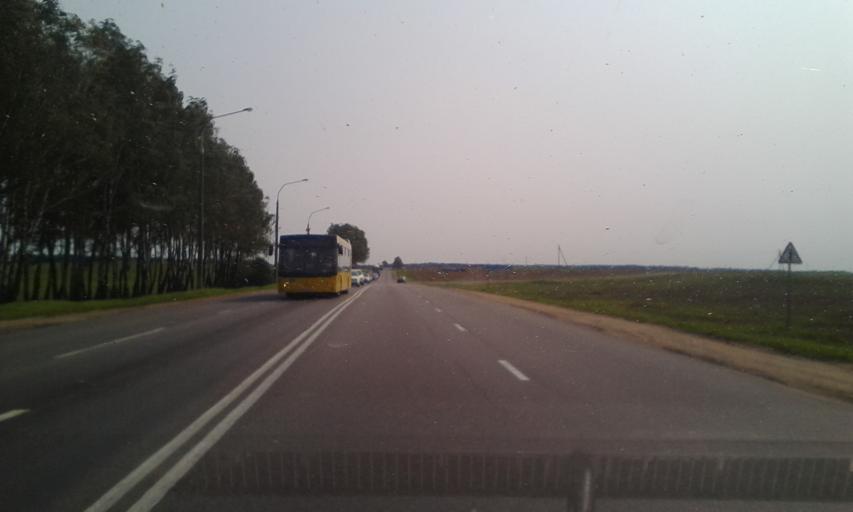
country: BY
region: Minsk
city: Machulishchy
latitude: 53.8311
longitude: 27.6122
